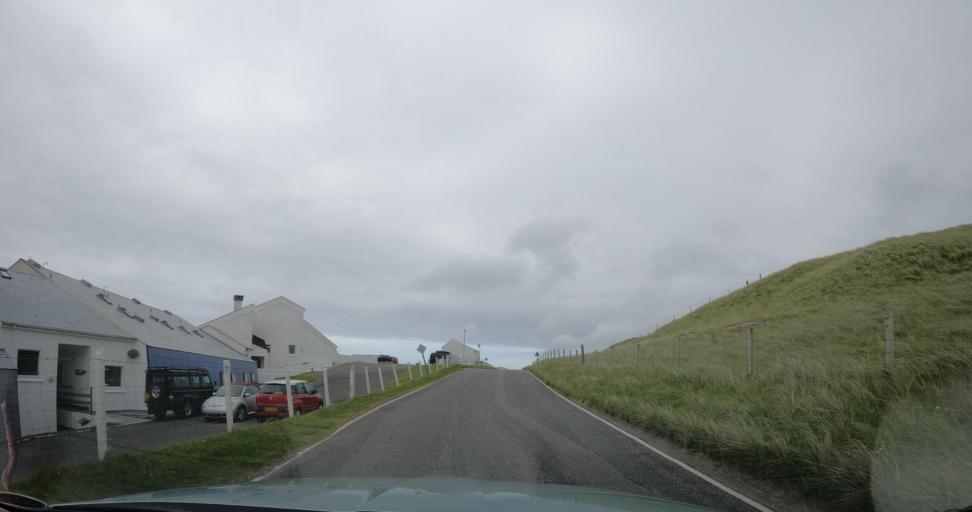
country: GB
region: Scotland
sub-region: Eilean Siar
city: Barra
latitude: 56.9755
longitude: -7.5176
